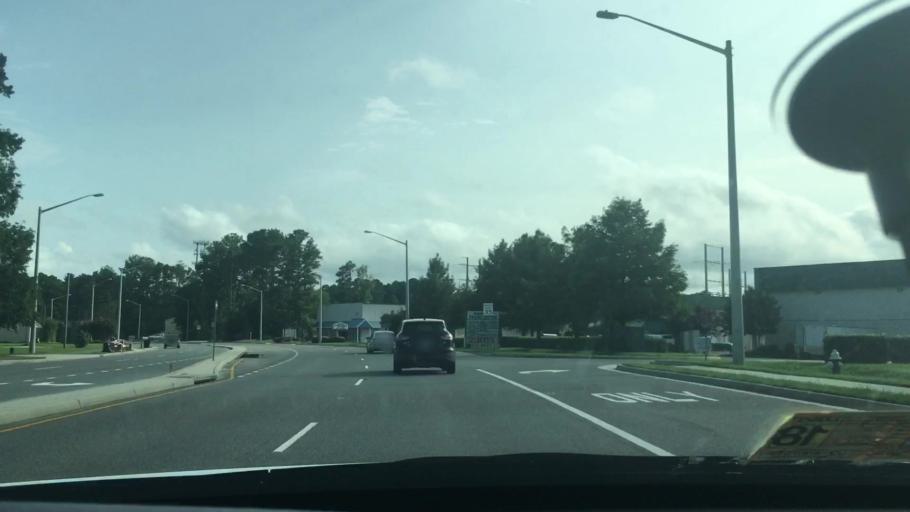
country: US
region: Virginia
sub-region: City of Virginia Beach
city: Virginia Beach
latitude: 36.8234
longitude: -75.9998
